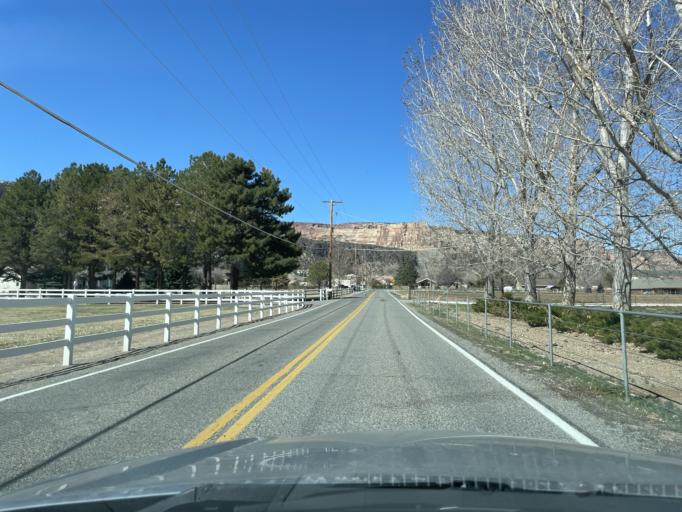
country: US
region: Colorado
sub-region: Mesa County
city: Redlands
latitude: 39.0742
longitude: -108.6609
